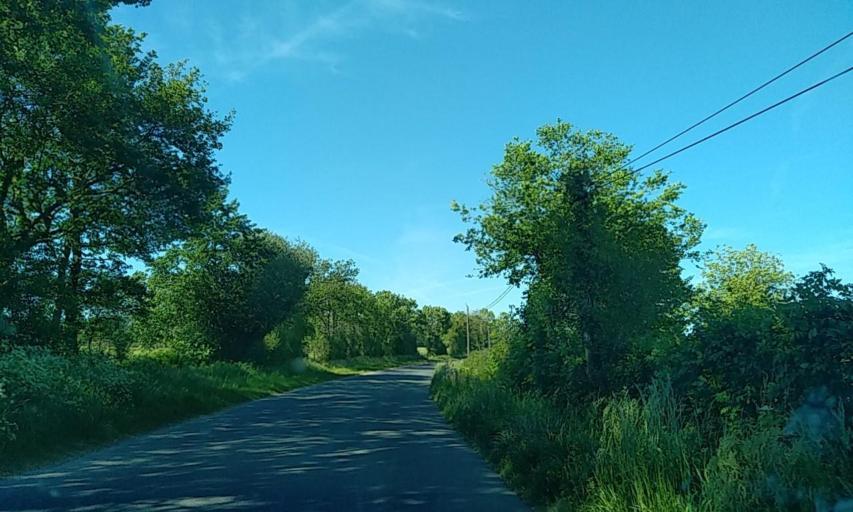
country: FR
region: Poitou-Charentes
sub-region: Departement des Deux-Sevres
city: Boisme
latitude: 46.8010
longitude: -0.4213
